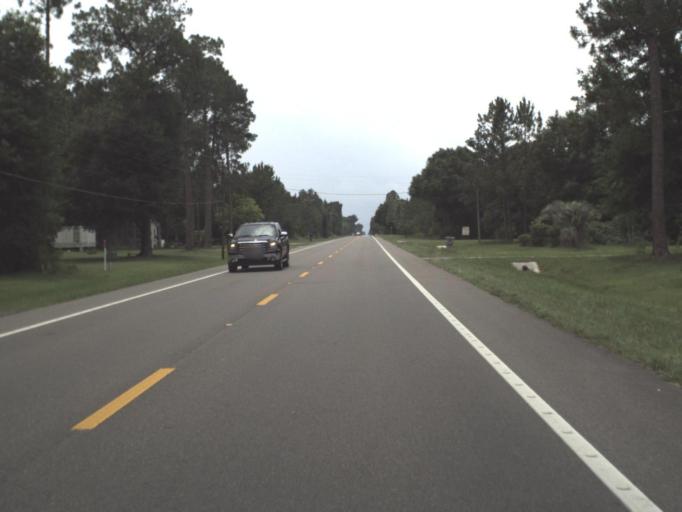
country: US
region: Florida
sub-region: Bradford County
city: Starke
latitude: 29.9079
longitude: -82.0916
